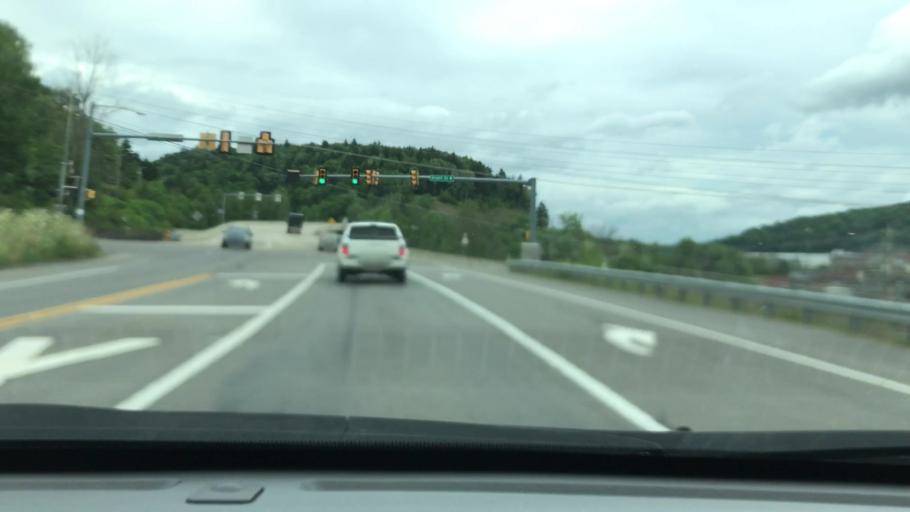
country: US
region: Pennsylvania
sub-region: Elk County
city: Johnsonburg
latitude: 41.4854
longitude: -78.6783
